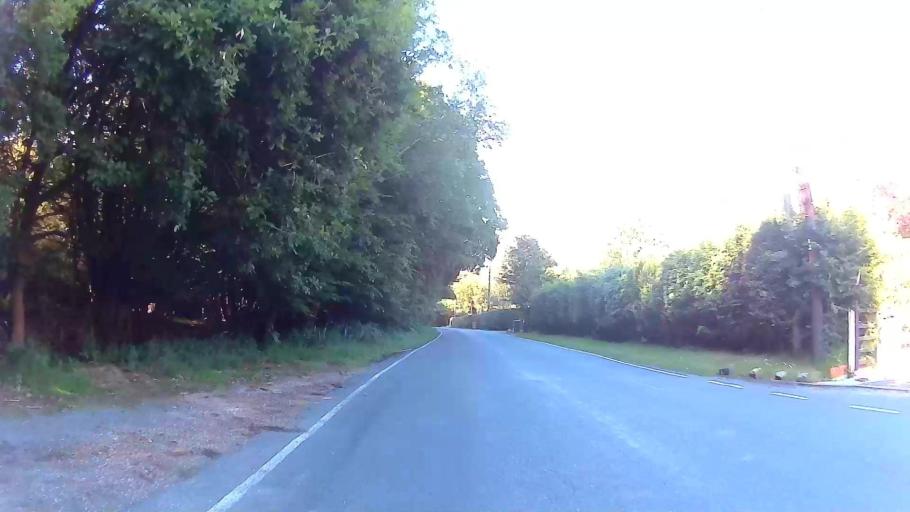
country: GB
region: England
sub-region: Essex
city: Ingatestone
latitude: 51.6963
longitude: 0.3457
